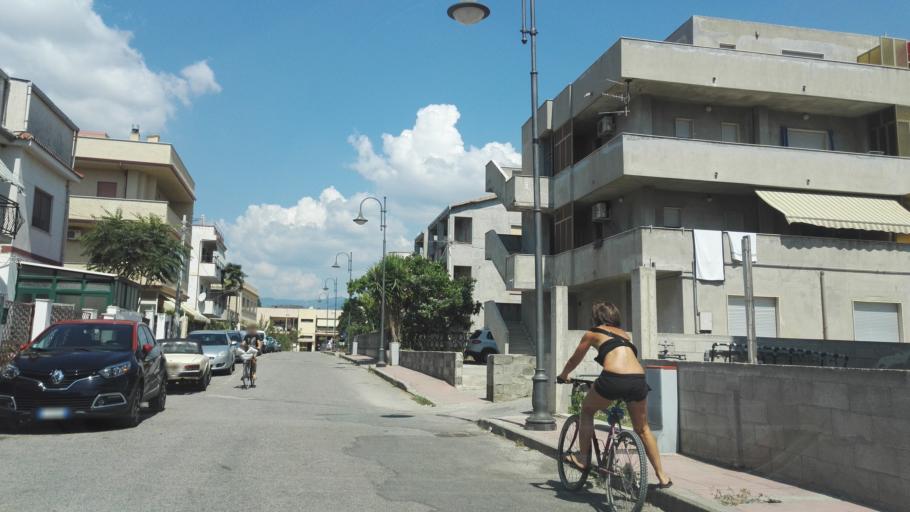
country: IT
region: Calabria
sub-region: Provincia di Reggio Calabria
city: Caulonia Marina
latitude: 38.3405
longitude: 16.4638
